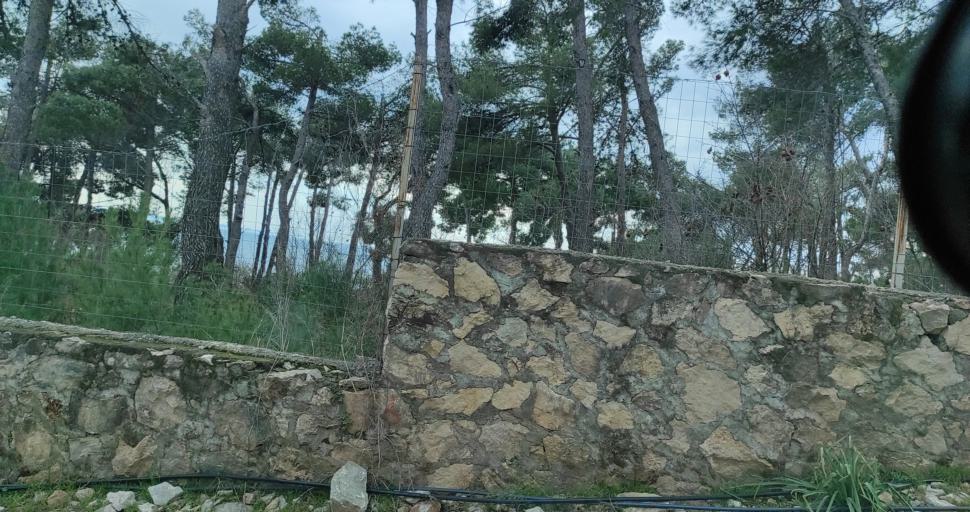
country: AL
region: Lezhe
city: Shengjin
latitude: 41.8123
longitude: 19.5831
